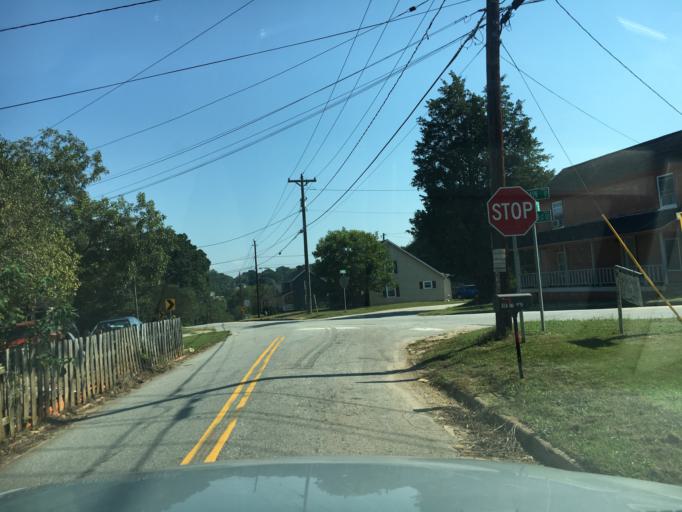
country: US
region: South Carolina
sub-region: Spartanburg County
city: Wellford
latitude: 34.9262
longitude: -82.1030
